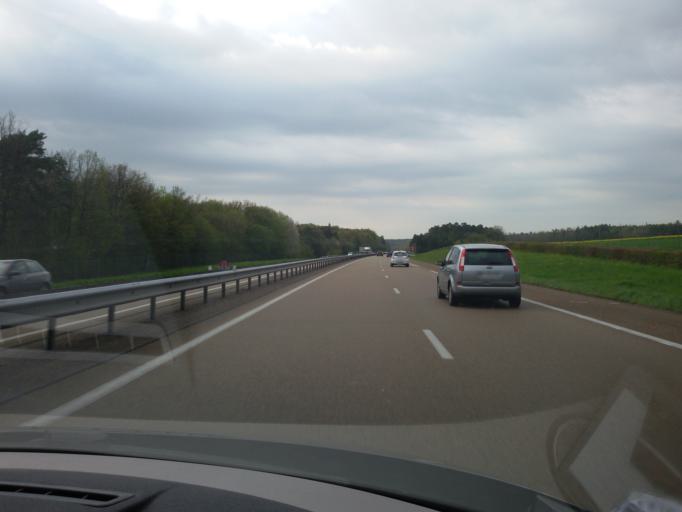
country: FR
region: Champagne-Ardenne
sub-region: Departement de la Haute-Marne
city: Chamarandes-Choignes
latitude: 47.9830
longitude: 5.1311
